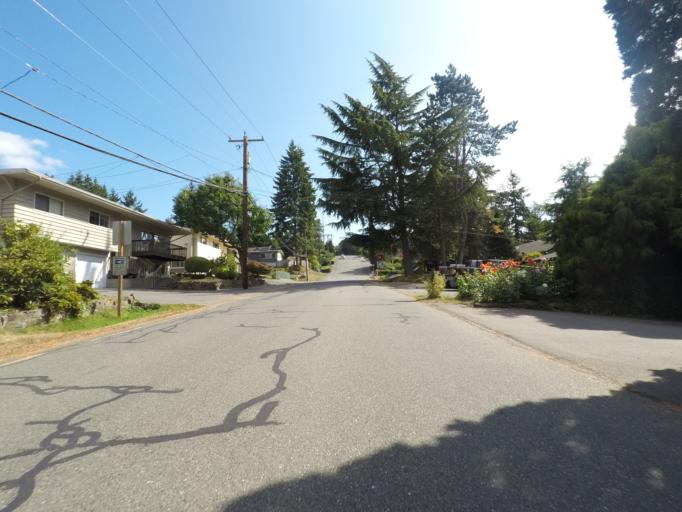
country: US
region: Washington
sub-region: Snohomish County
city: Brier
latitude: 47.7714
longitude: -122.2600
